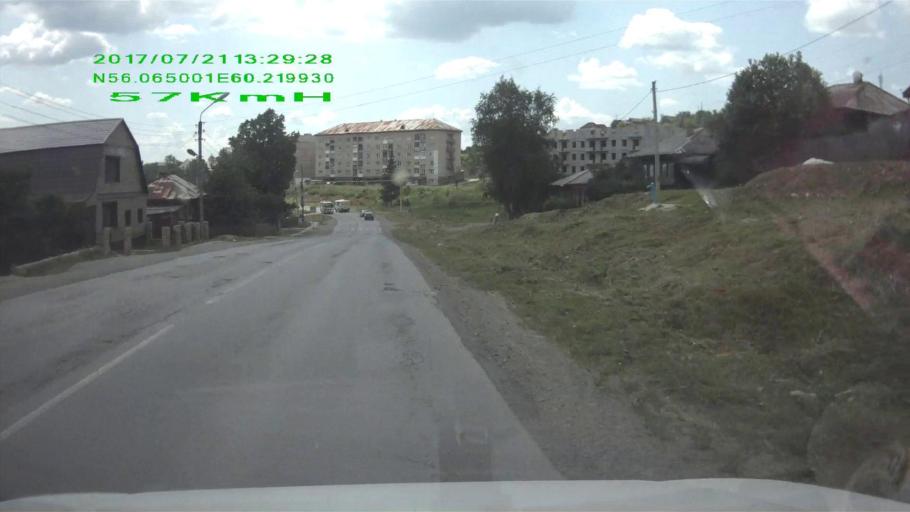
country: RU
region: Chelyabinsk
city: Verkhniy Ufaley
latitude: 56.0644
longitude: 60.2193
